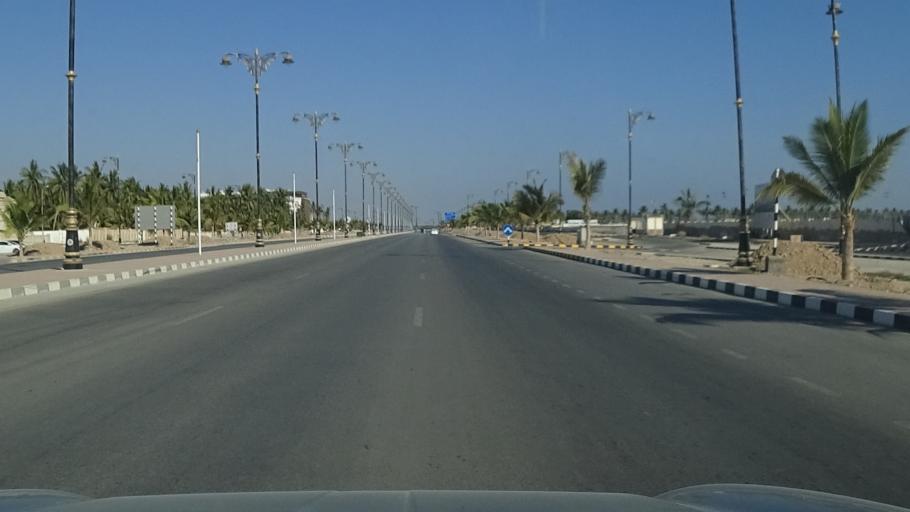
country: OM
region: Zufar
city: Salalah
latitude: 17.0360
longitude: 54.1650
